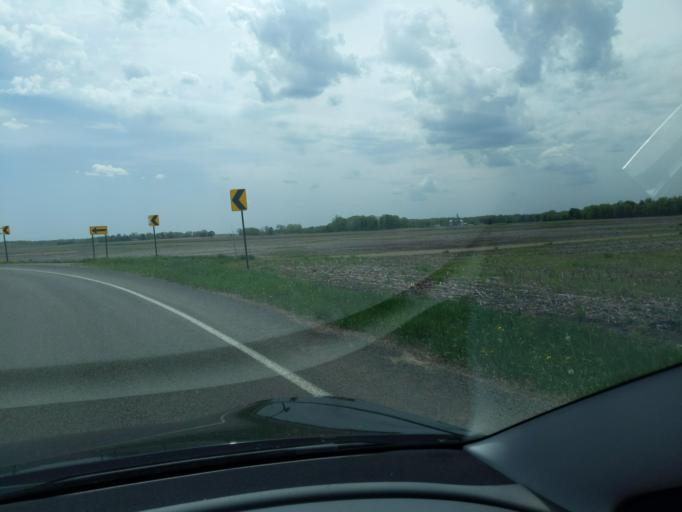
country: US
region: Michigan
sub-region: Ingham County
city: Stockbridge
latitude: 42.4831
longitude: -84.2780
